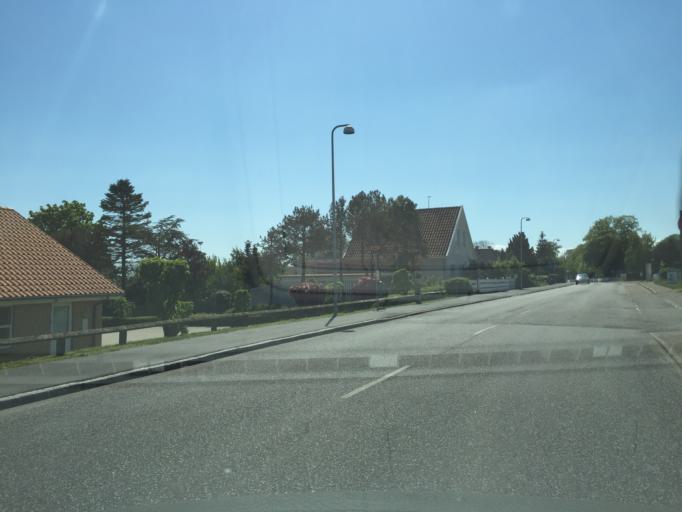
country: DK
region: Zealand
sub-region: Vordingborg Kommune
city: Stege
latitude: 54.9901
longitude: 12.2931
